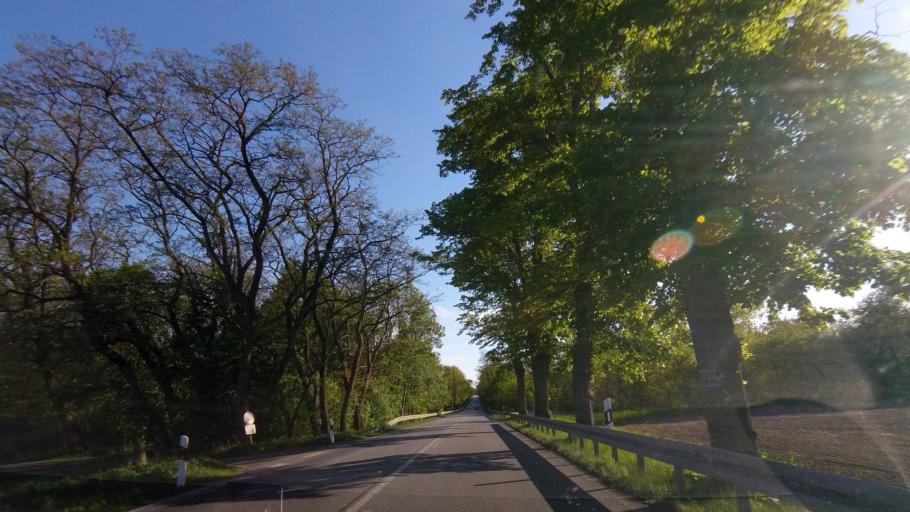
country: DE
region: Brandenburg
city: Luebben
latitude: 51.9202
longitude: 13.8720
